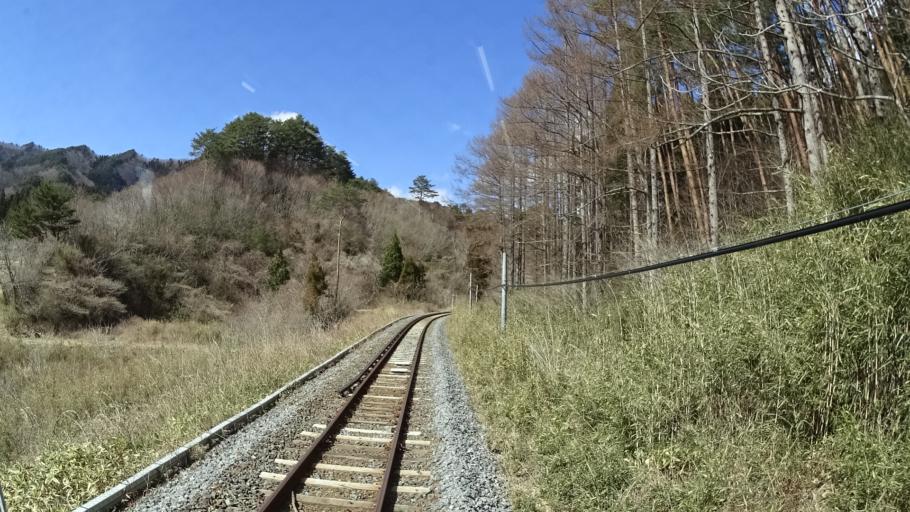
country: JP
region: Iwate
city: Yamada
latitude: 39.4894
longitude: 141.9237
